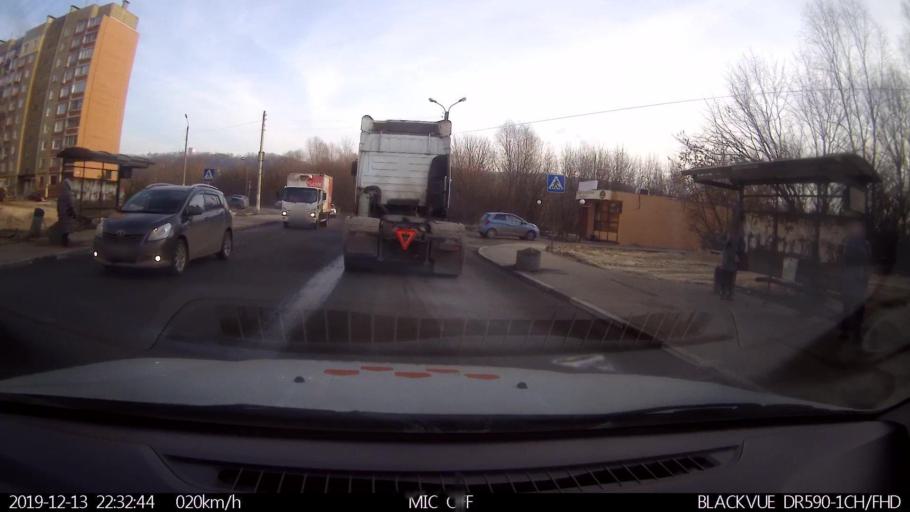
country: RU
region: Nizjnij Novgorod
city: Nizhniy Novgorod
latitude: 56.2851
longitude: 43.9515
